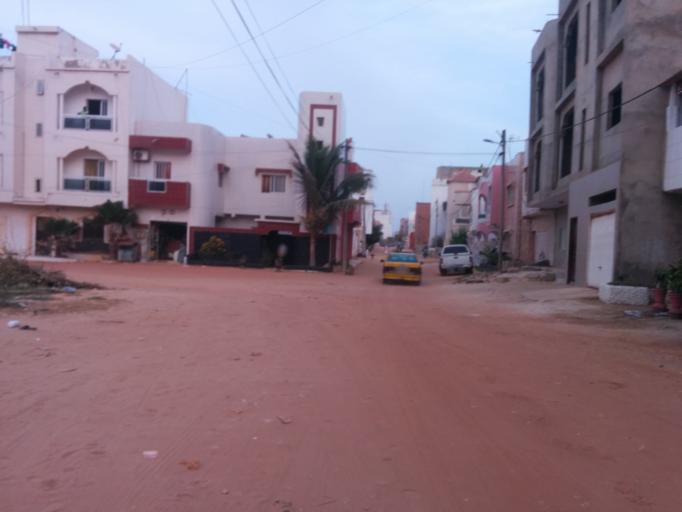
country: SN
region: Dakar
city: Grand Dakar
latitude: 14.7620
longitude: -17.4546
